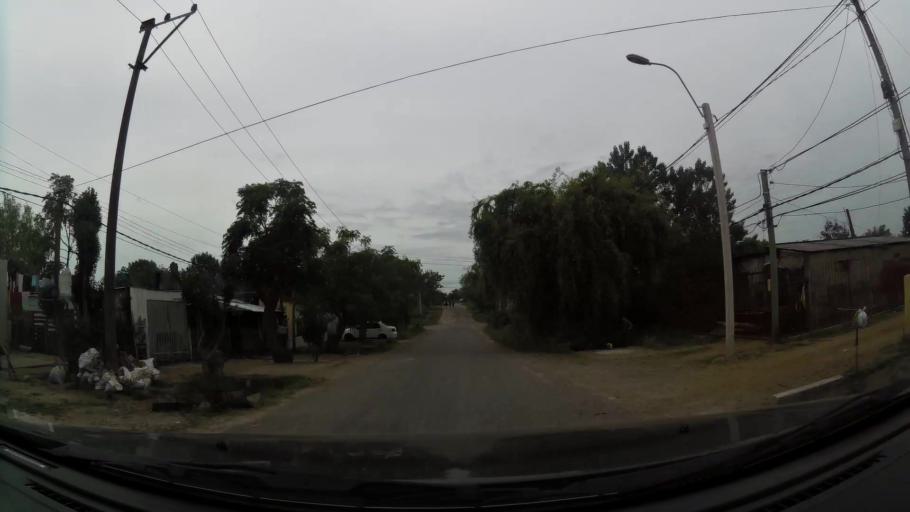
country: UY
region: Canelones
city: Las Piedras
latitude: -34.7317
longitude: -56.2074
